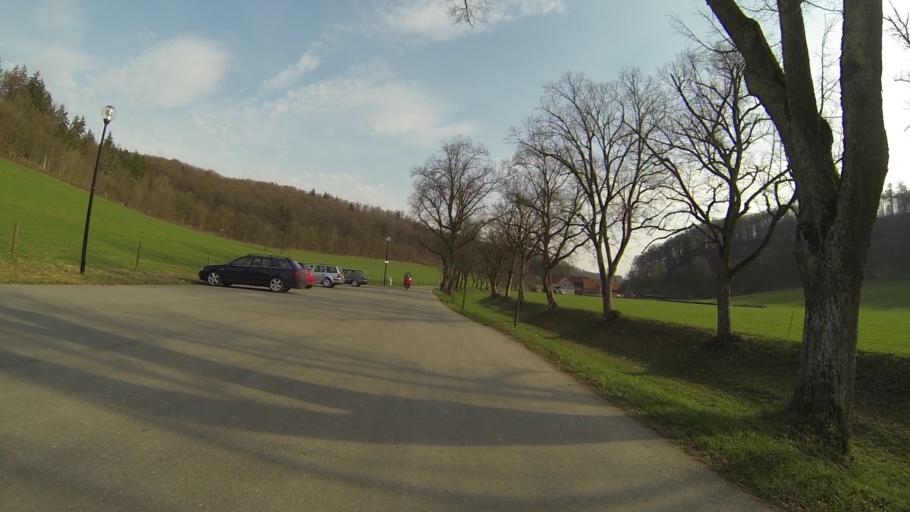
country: DE
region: Baden-Wuerttemberg
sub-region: Regierungsbezirk Stuttgart
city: Heidenheim an der Brenz
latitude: 48.6746
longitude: 10.1325
